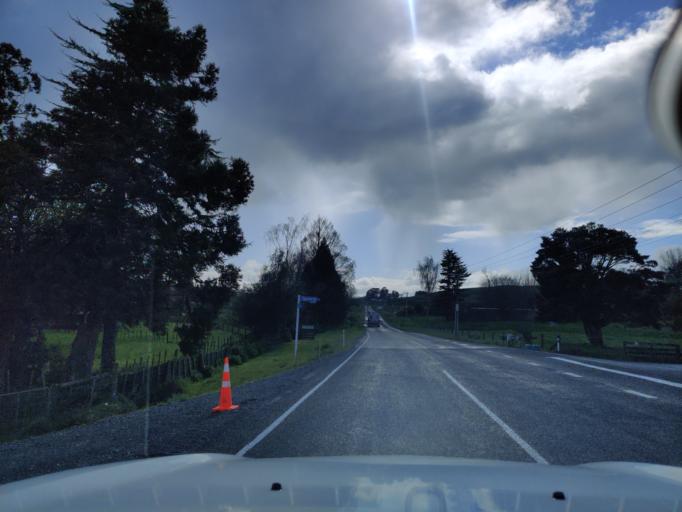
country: NZ
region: Waikato
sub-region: Waikato District
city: Ngaruawahia
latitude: -37.5947
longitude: 175.2071
